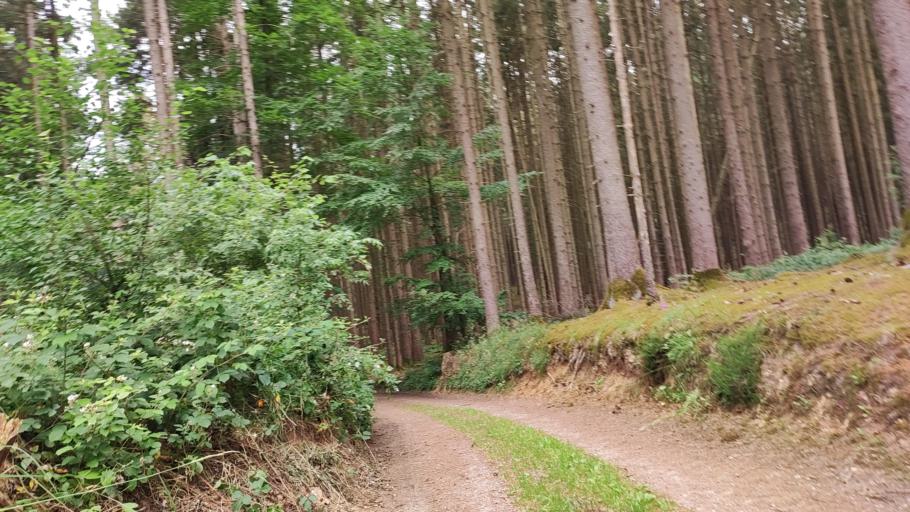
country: DE
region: Bavaria
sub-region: Swabia
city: Horgau
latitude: 48.4123
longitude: 10.6949
